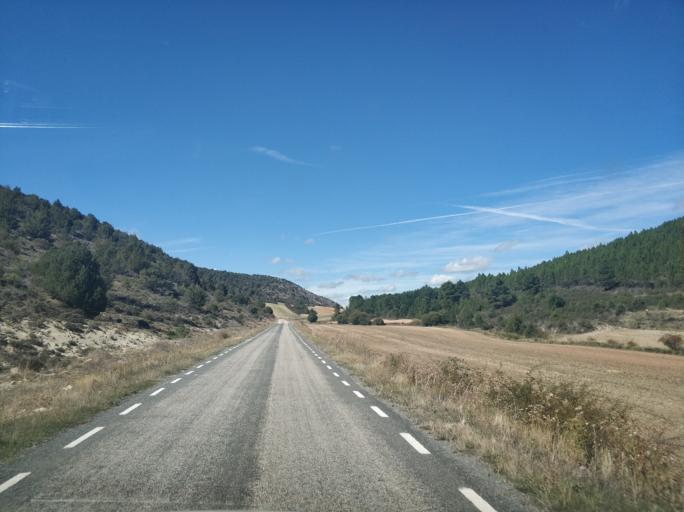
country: ES
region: Castille and Leon
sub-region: Provincia de Soria
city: Espeja de San Marcelino
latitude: 41.8152
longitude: -3.2319
